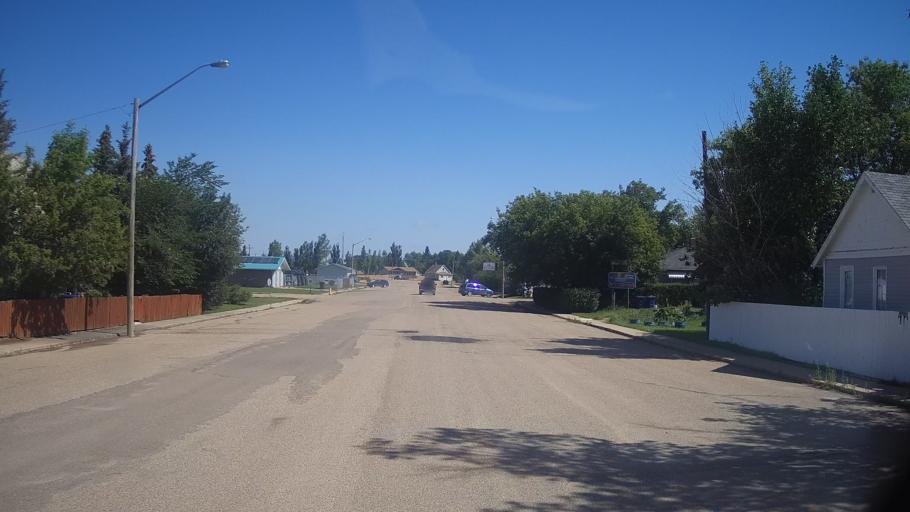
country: CA
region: Saskatchewan
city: Saskatoon
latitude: 51.8942
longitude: -106.0555
